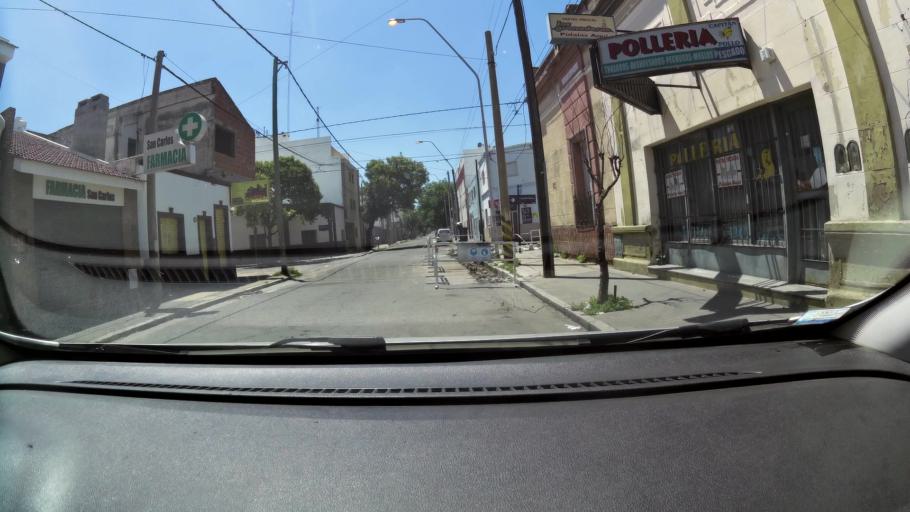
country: AR
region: Cordoba
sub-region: Departamento de Capital
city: Cordoba
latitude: -31.3859
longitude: -64.1997
